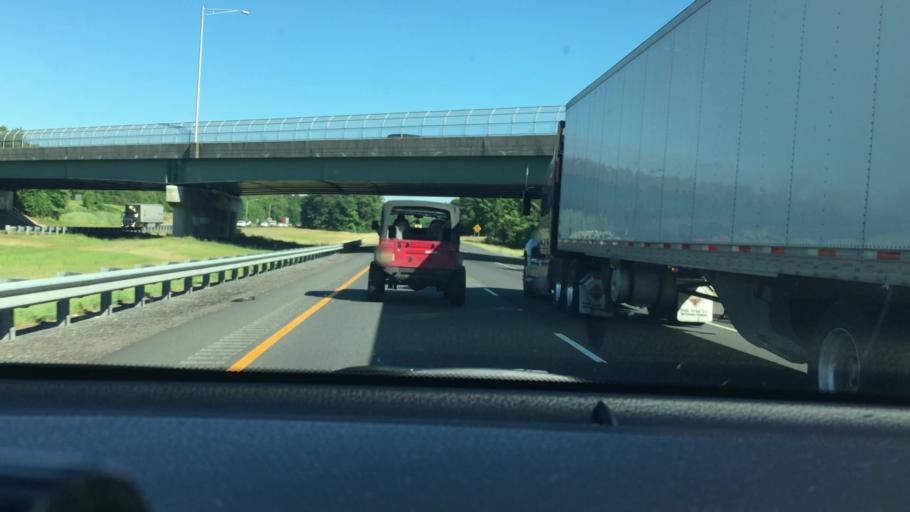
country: US
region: New Jersey
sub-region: Gloucester County
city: Richwood
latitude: 39.6972
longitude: -75.1468
